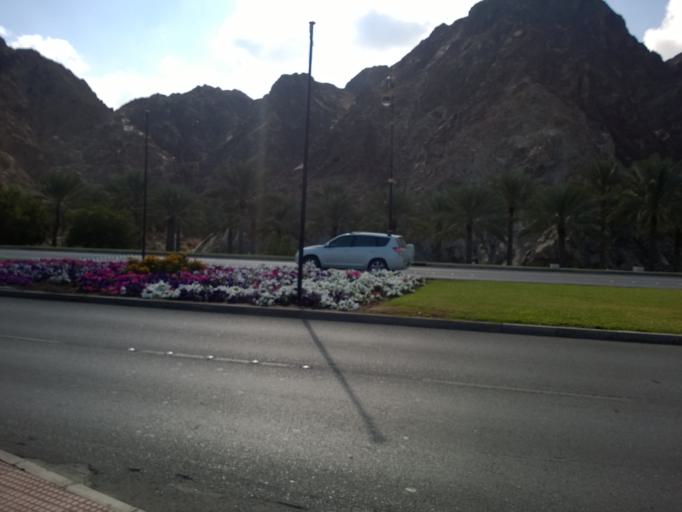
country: OM
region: Muhafazat Masqat
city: Muscat
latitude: 23.6220
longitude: 58.5744
